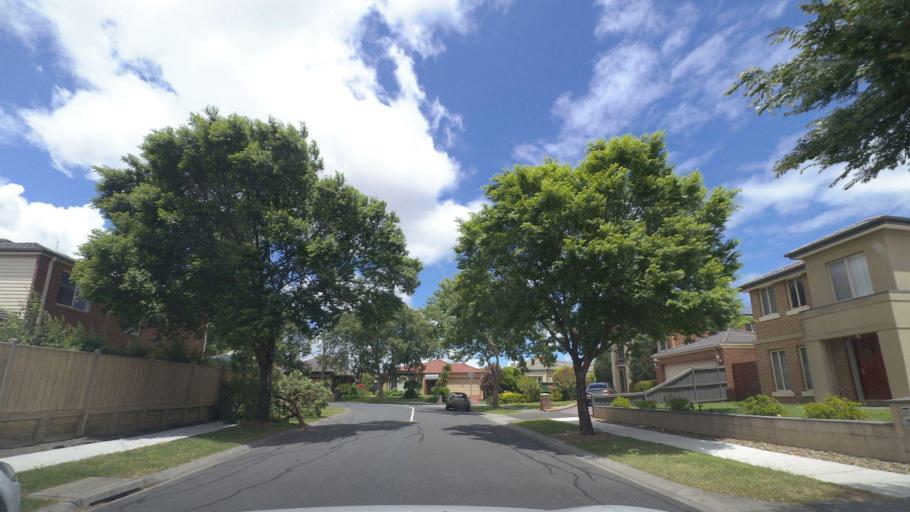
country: AU
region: Victoria
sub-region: Knox
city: Ferntree Gully
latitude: -37.9029
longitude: 145.2756
